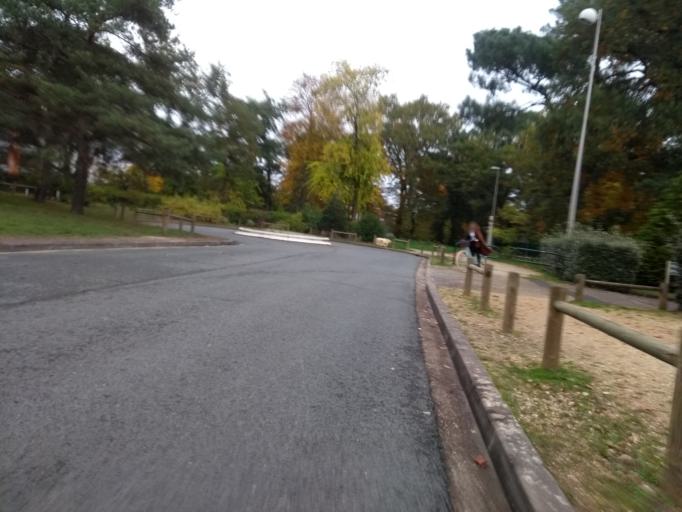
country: FR
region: Aquitaine
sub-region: Departement de la Gironde
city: Gradignan
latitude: 44.7750
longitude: -0.6080
